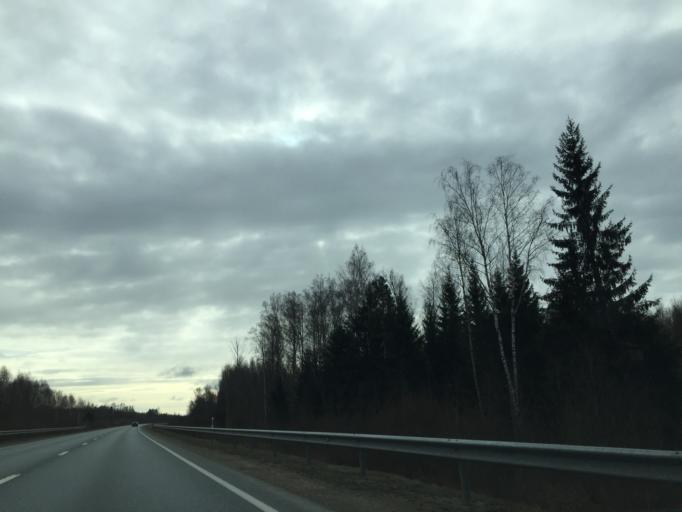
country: LV
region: Koknese
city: Koknese
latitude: 56.6963
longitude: 25.3385
